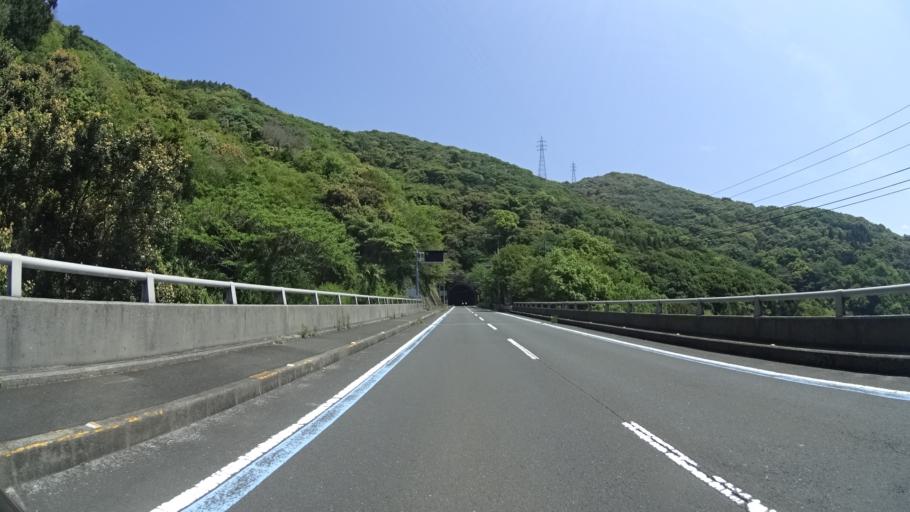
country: JP
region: Ehime
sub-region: Nishiuwa-gun
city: Ikata-cho
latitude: 33.4504
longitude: 132.2709
